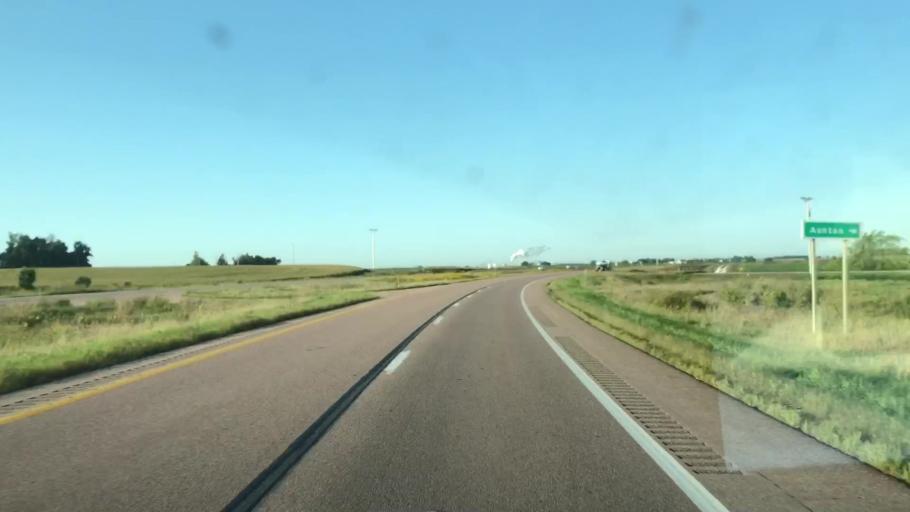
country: US
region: Iowa
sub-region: Osceola County
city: Sibley
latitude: 43.3062
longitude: -95.7806
